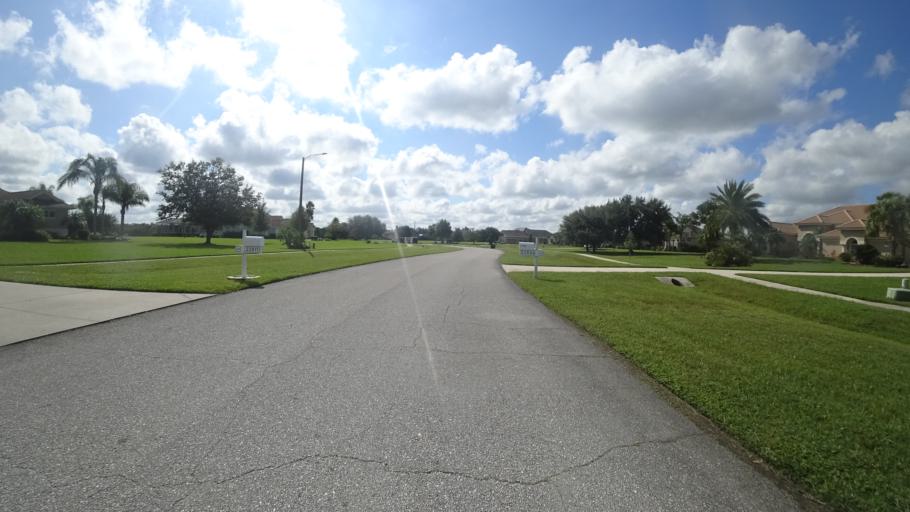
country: US
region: Florida
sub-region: Sarasota County
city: Fruitville
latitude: 27.3933
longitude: -82.3098
